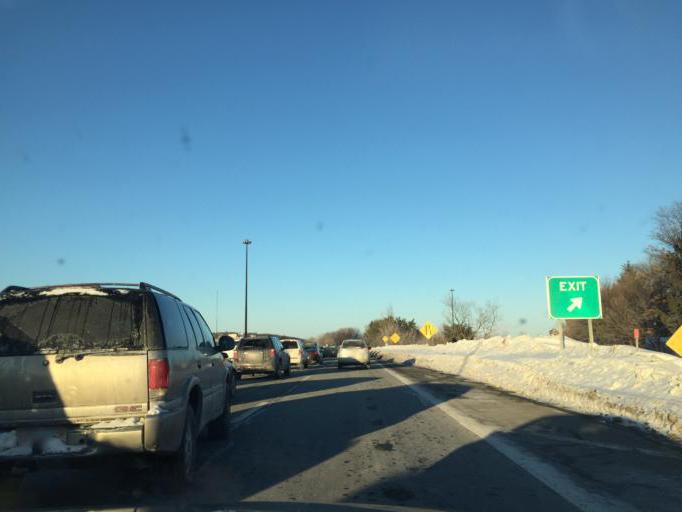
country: US
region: Massachusetts
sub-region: Suffolk County
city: Revere
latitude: 42.4278
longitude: -71.0199
